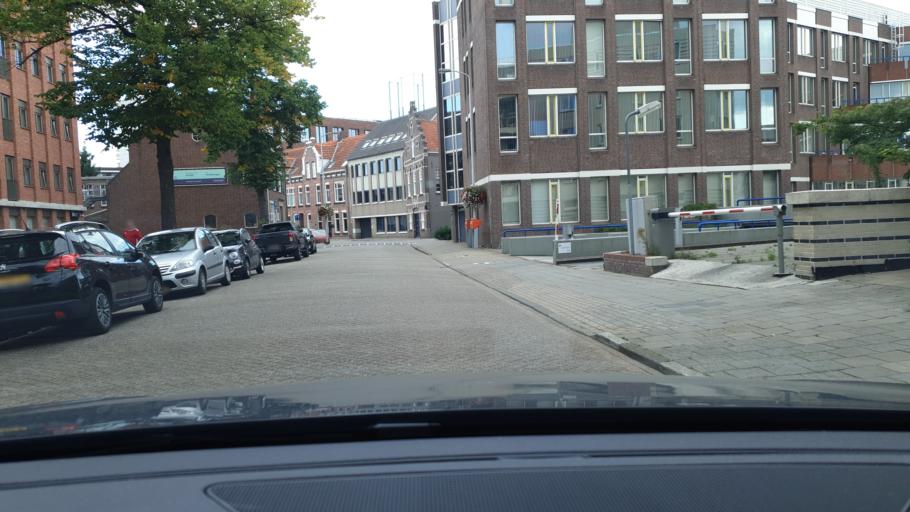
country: NL
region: North Brabant
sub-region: Gemeente Eindhoven
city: Eindhoven
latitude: 51.4349
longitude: 5.4784
